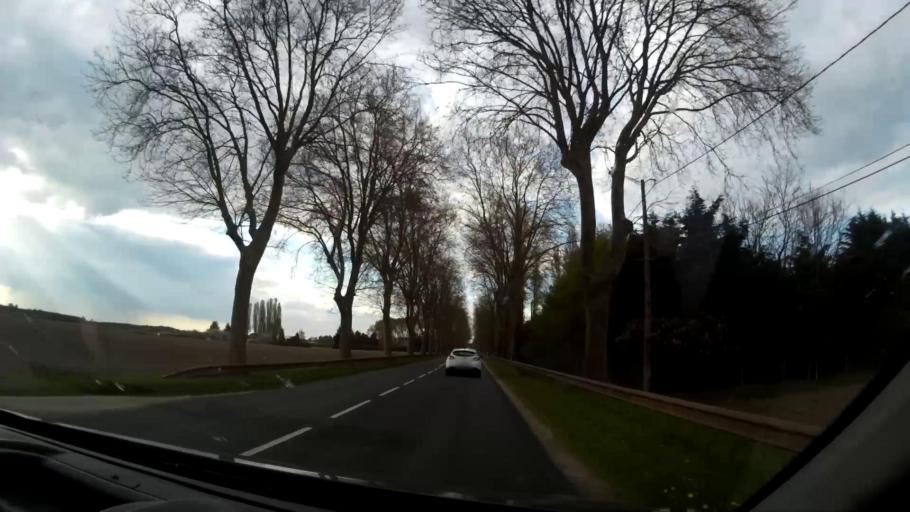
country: FR
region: Centre
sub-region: Departement du Loir-et-Cher
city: Cormeray
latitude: 47.4812
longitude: 1.4147
